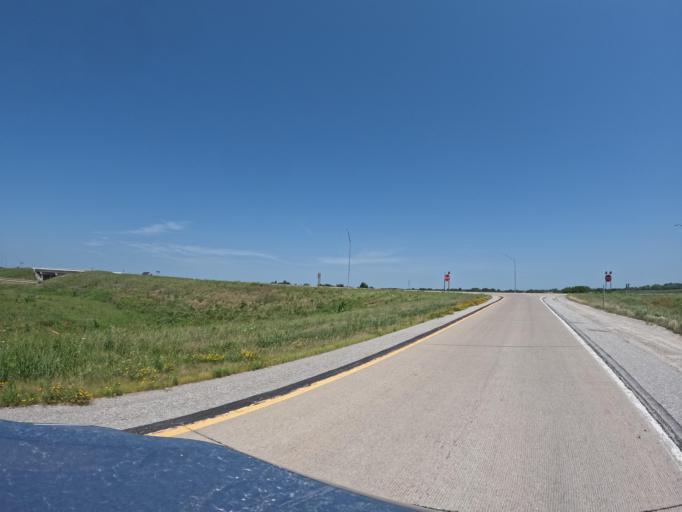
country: US
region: Iowa
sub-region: Henry County
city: Mount Pleasant
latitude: 40.9370
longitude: -91.5321
